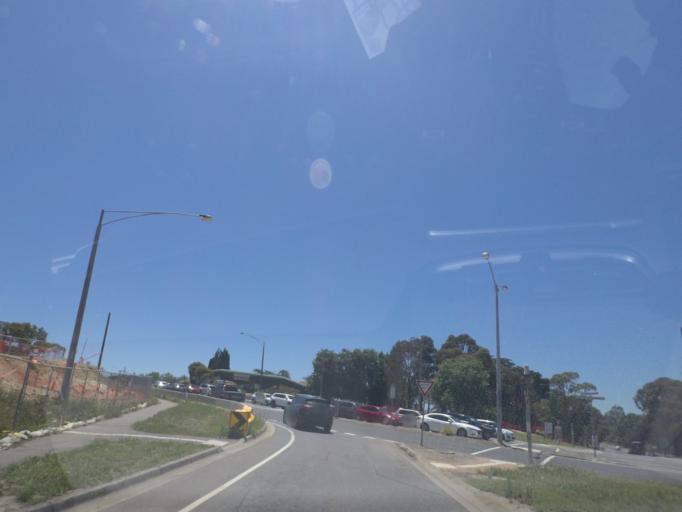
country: AU
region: Victoria
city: Plenty
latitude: -37.6778
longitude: 145.1253
